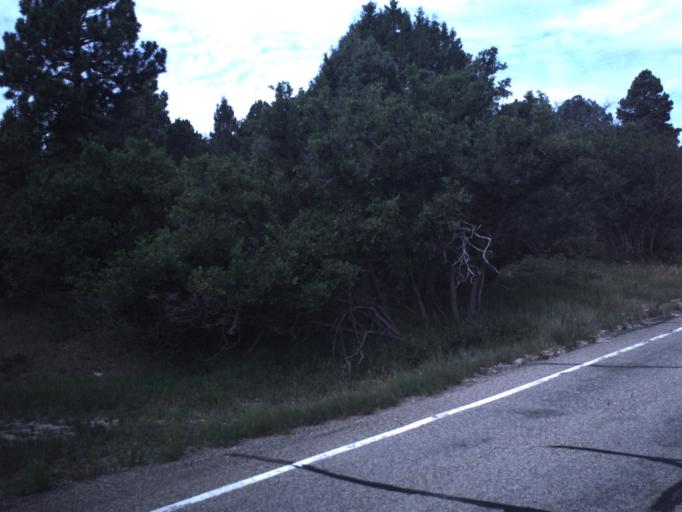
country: US
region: Utah
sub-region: Garfield County
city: Panguitch
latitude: 37.4969
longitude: -112.5446
